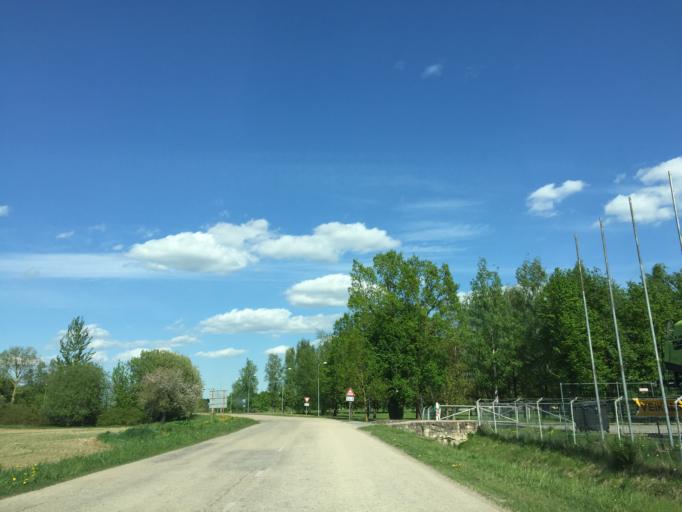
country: LV
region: Bauskas Rajons
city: Bauska
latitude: 56.3964
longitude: 24.1227
